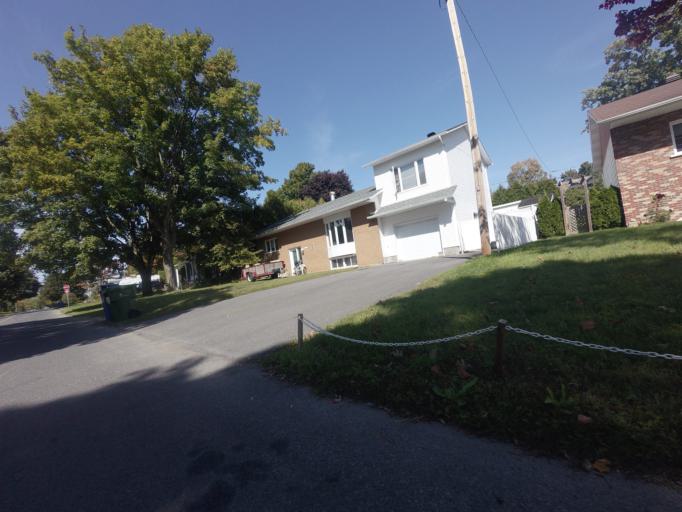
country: CA
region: Quebec
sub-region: Laurentides
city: Saint-Eustache
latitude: 45.5555
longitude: -73.9072
